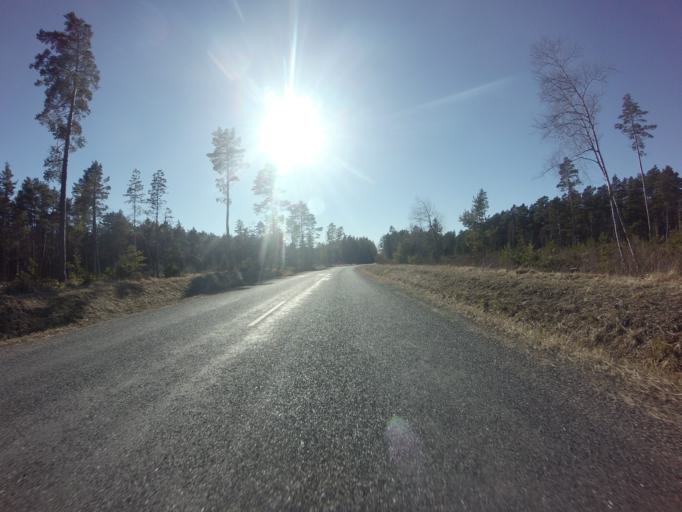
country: EE
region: Saare
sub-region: Kuressaare linn
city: Kuressaare
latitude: 58.5863
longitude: 22.5686
